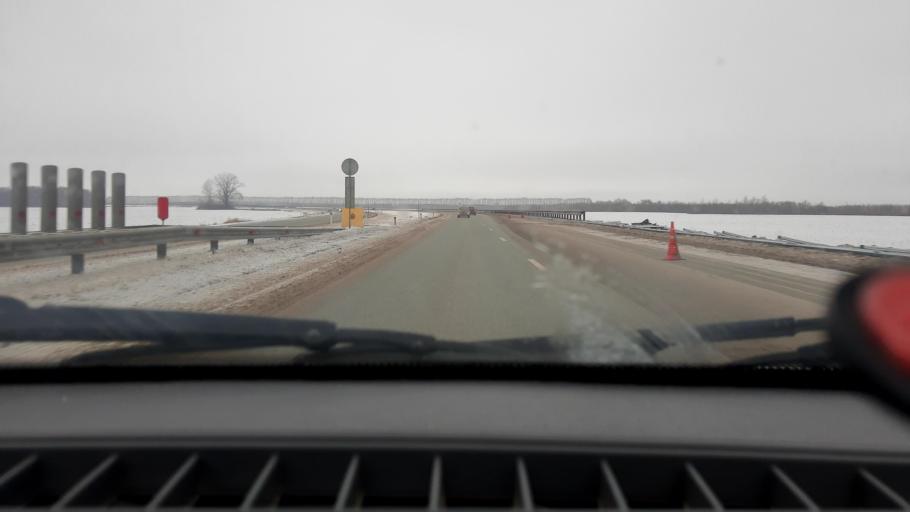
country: RU
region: Bashkortostan
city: Asanovo
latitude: 54.9773
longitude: 55.5691
